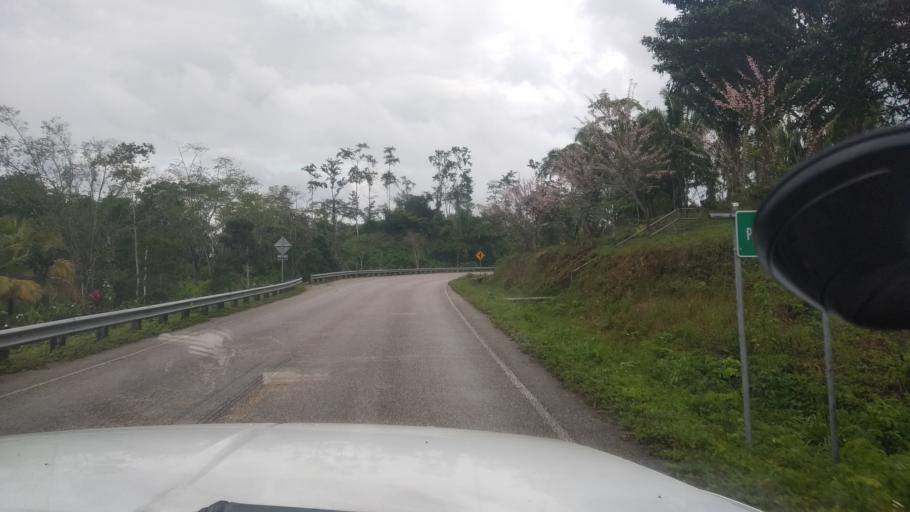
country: GT
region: Peten
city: San Luis
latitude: 16.2014
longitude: -89.1468
